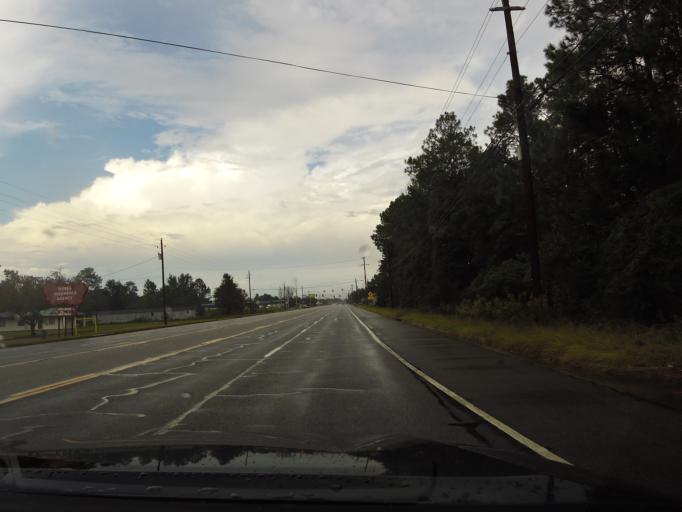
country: US
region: Georgia
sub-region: Wayne County
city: Jesup
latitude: 31.6455
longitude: -81.8567
